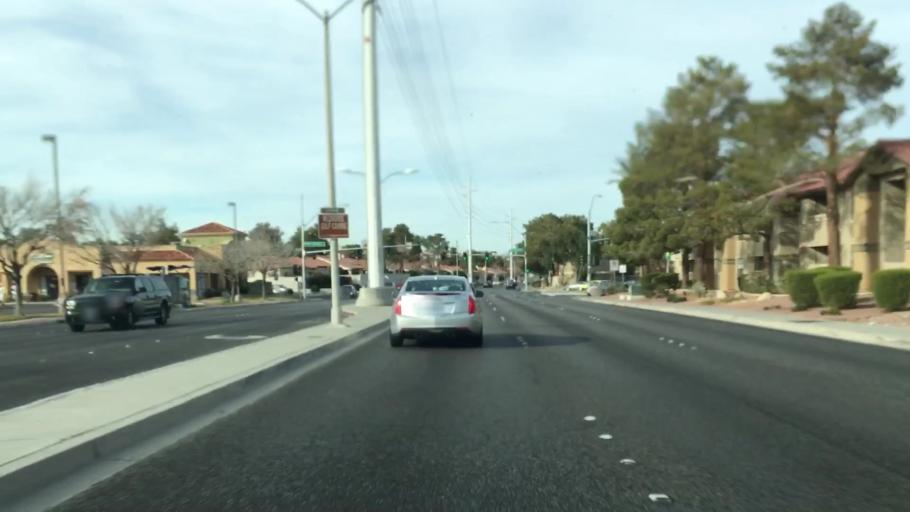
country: US
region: Nevada
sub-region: Clark County
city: Whitney
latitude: 36.0555
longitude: -115.0836
